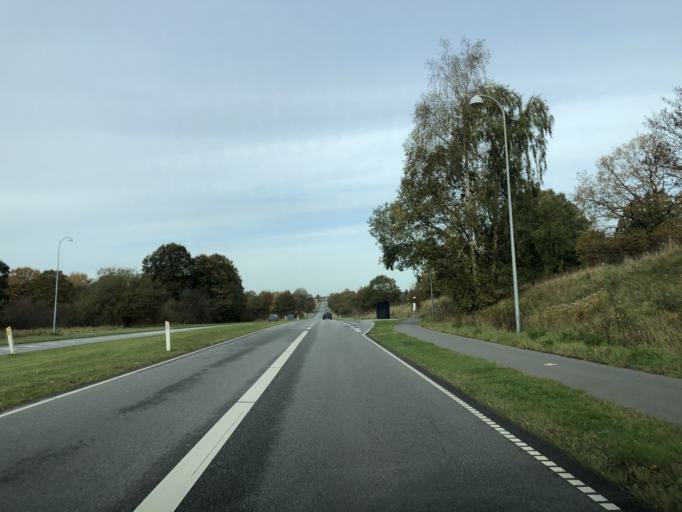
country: DK
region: Capital Region
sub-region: Allerod Kommune
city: Blovstrod
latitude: 55.8580
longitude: 12.4032
